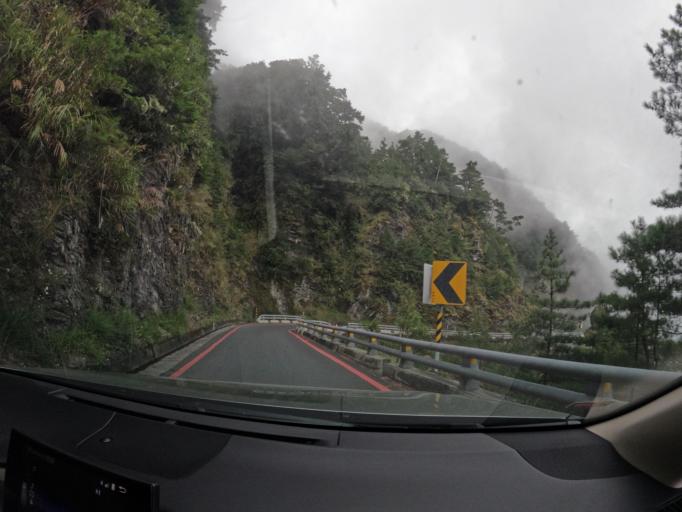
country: TW
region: Taiwan
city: Lugu
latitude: 23.2654
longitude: 120.9773
